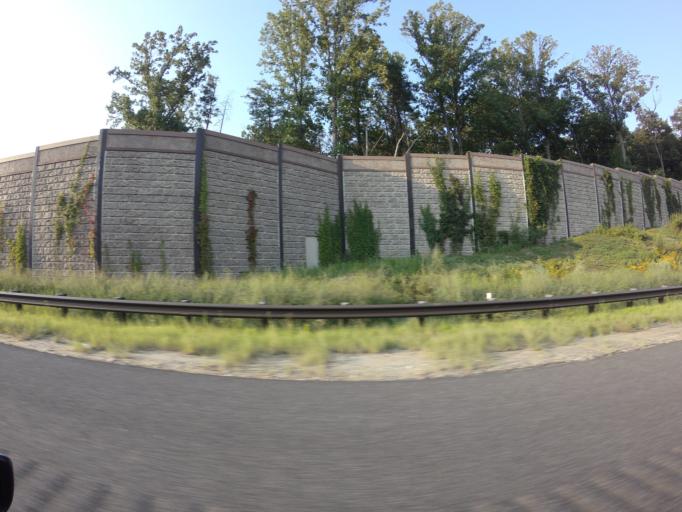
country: US
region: Maryland
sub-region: Montgomery County
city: Fairland
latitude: 39.0838
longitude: -76.9703
